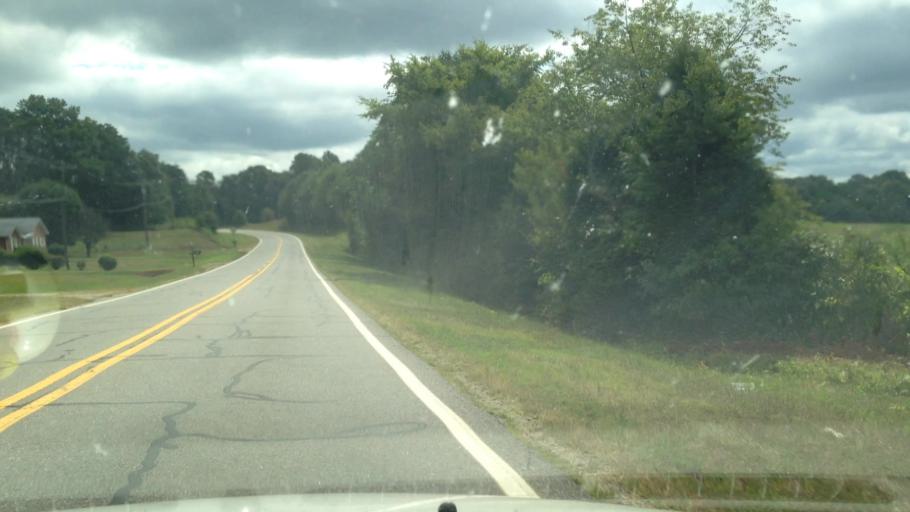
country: US
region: North Carolina
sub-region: Rockingham County
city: Madison
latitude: 36.3753
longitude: -79.9358
